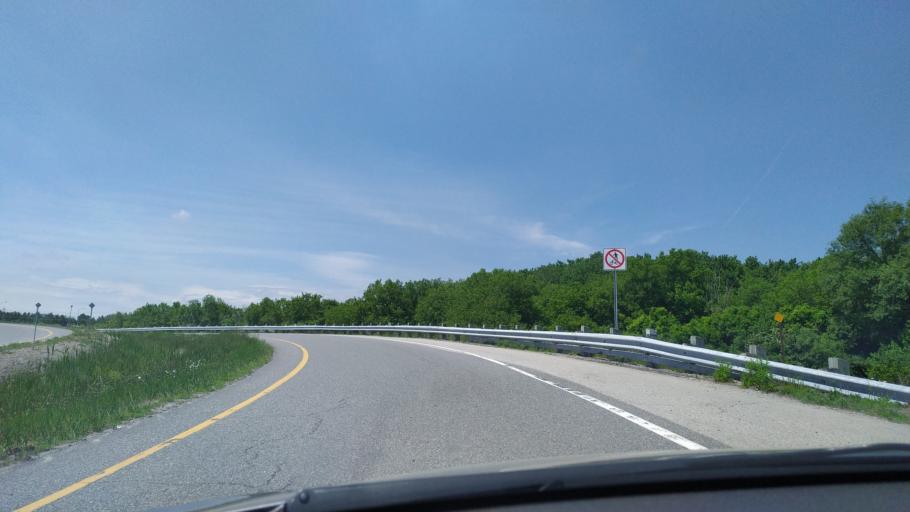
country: CA
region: Ontario
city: Ingersoll
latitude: 42.9773
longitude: -80.9516
